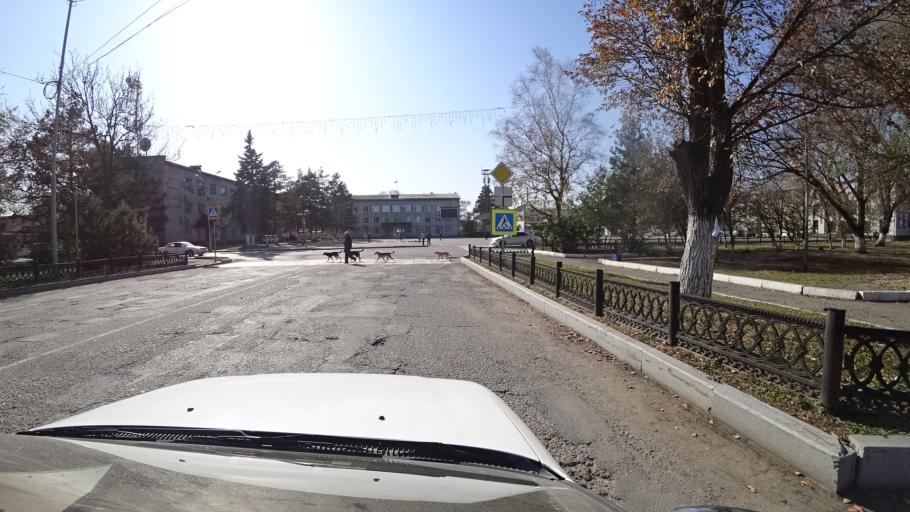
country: RU
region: Primorskiy
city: Dal'nerechensk
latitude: 45.9312
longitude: 133.7279
